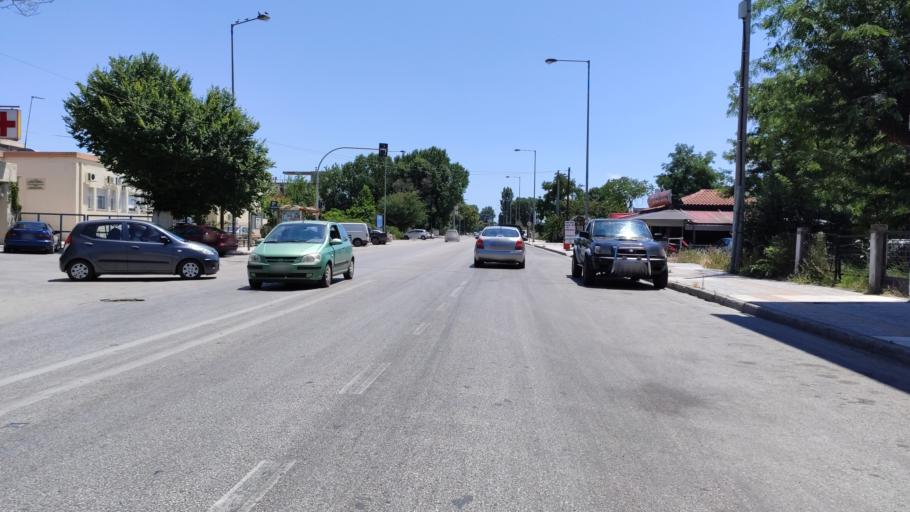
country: GR
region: East Macedonia and Thrace
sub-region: Nomos Rodopis
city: Komotini
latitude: 41.1124
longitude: 25.4115
